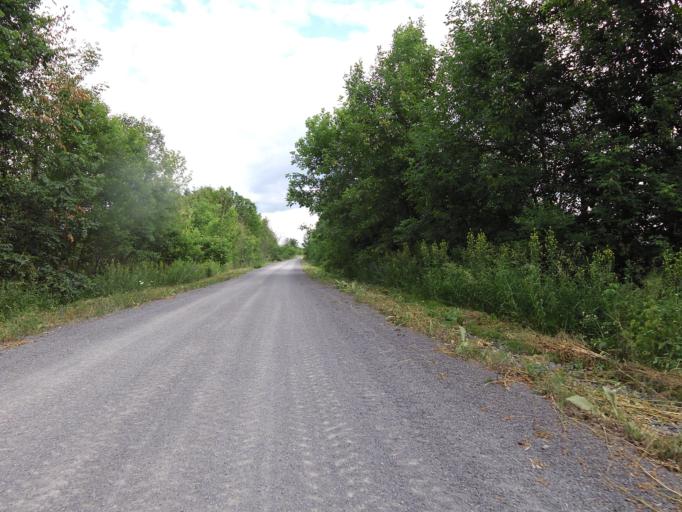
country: CA
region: Ontario
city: Carleton Place
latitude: 45.2830
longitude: -76.2467
